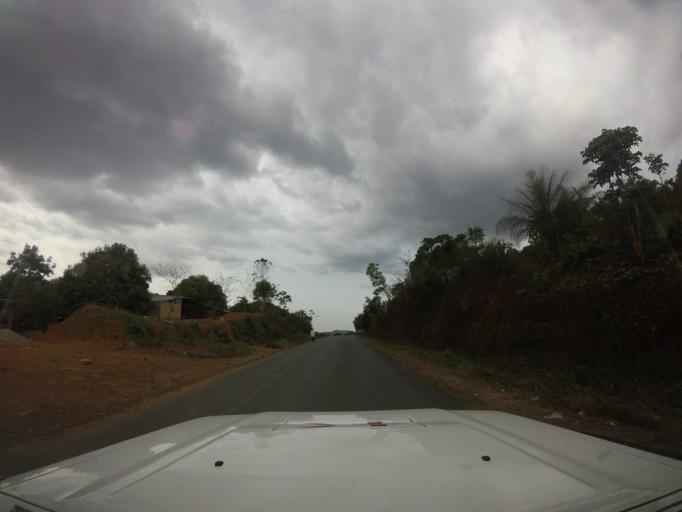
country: LR
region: Bomi
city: Tubmanburg
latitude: 6.8530
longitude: -10.8178
